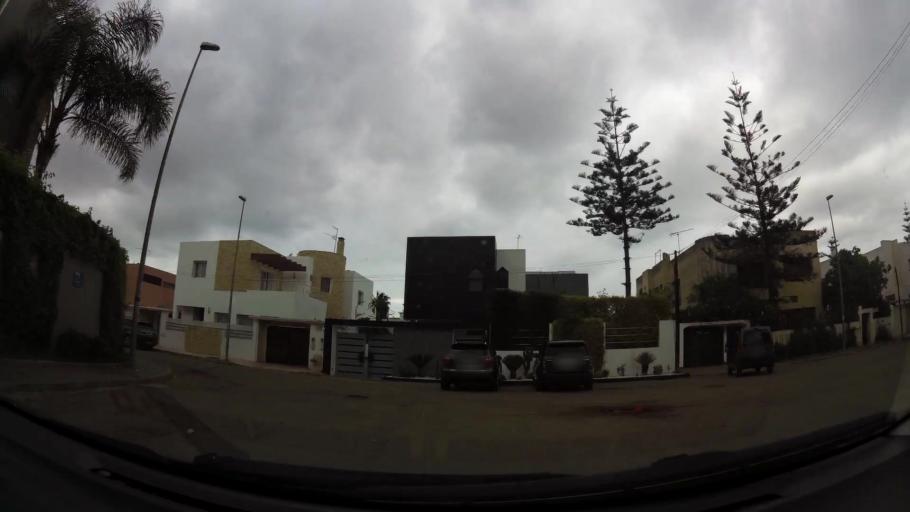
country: MA
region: Grand Casablanca
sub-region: Casablanca
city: Casablanca
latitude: 33.5701
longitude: -7.6591
